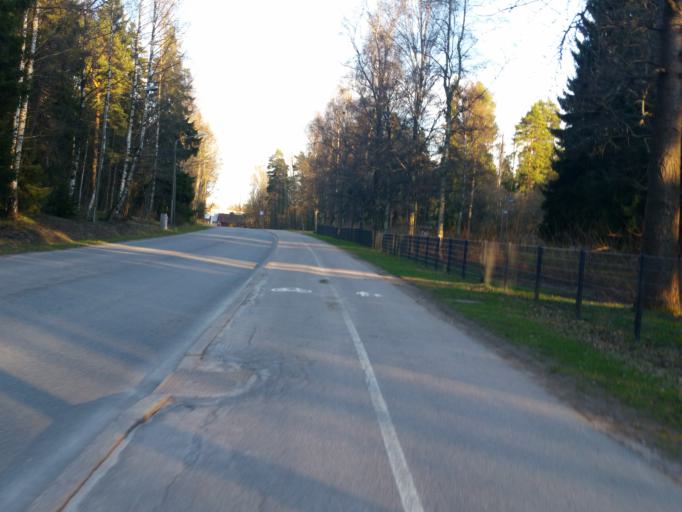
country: FI
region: Uusimaa
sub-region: Helsinki
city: Helsinki
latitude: 60.2122
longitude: 24.9598
